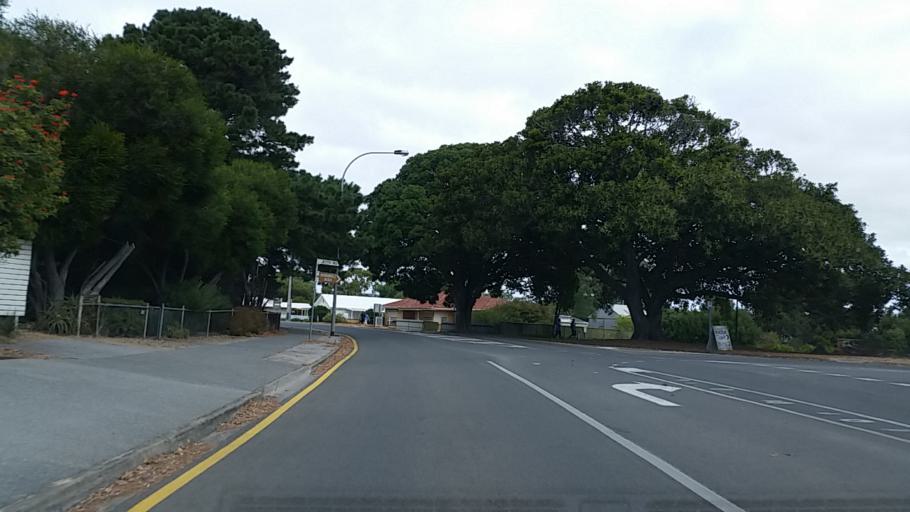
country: AU
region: South Australia
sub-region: Yankalilla
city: Normanville
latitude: -35.4445
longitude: 138.3162
